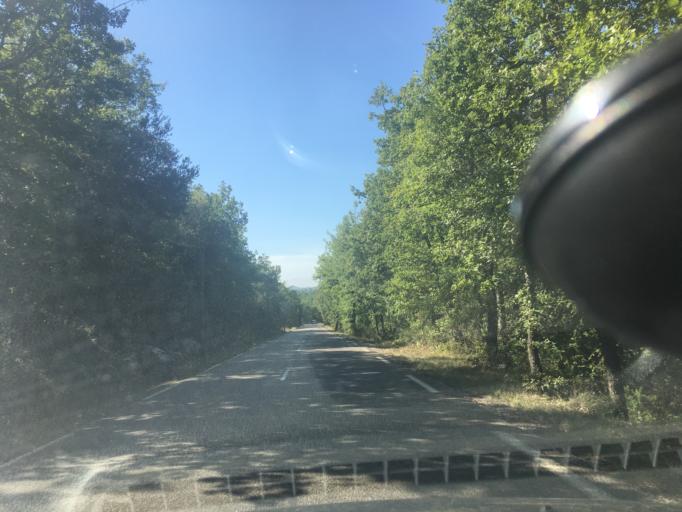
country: FR
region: Provence-Alpes-Cote d'Azur
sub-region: Departement du Var
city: Regusse
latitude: 43.6479
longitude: 6.0853
